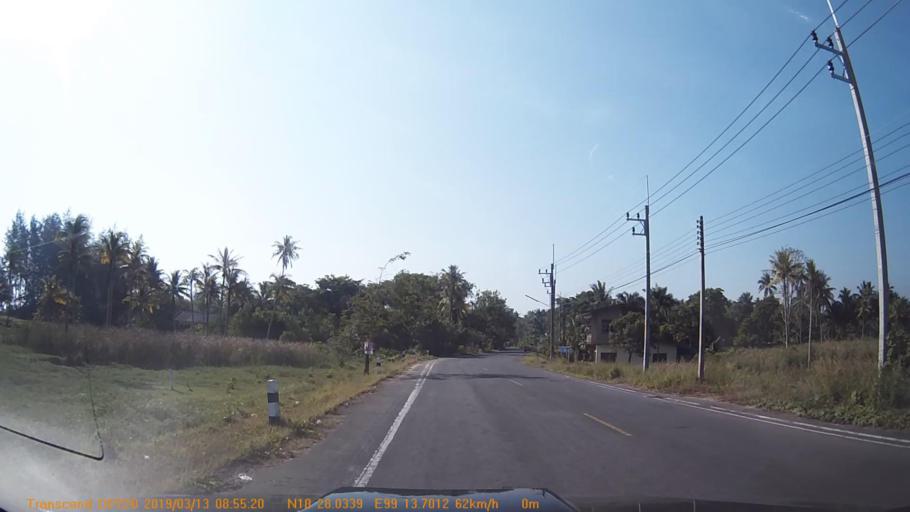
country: TH
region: Chumphon
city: Chumphon
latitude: 10.4670
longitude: 99.2284
